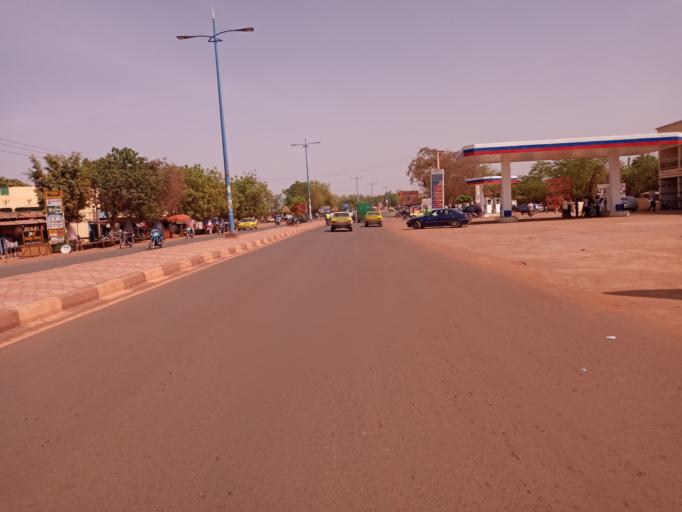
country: ML
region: Bamako
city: Bamako
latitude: 12.5793
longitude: -7.9877
